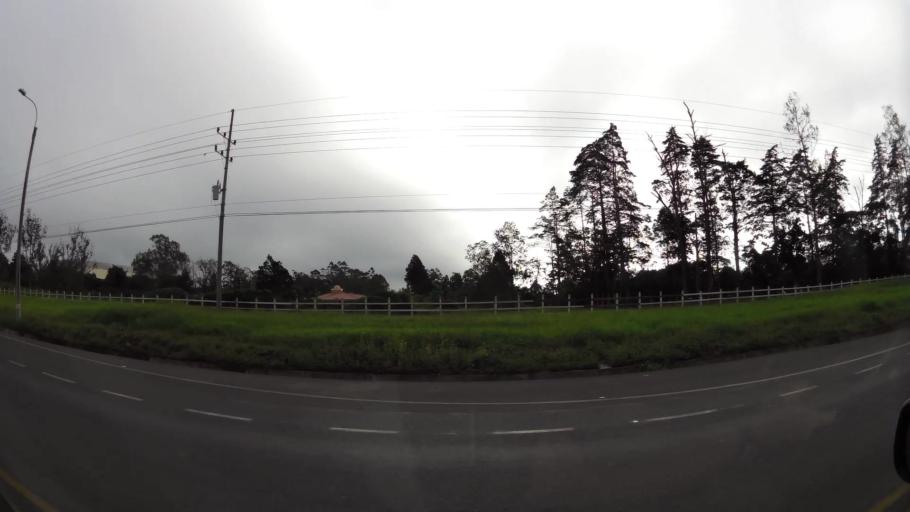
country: CR
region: Cartago
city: Cartago
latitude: 9.8645
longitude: -83.9459
